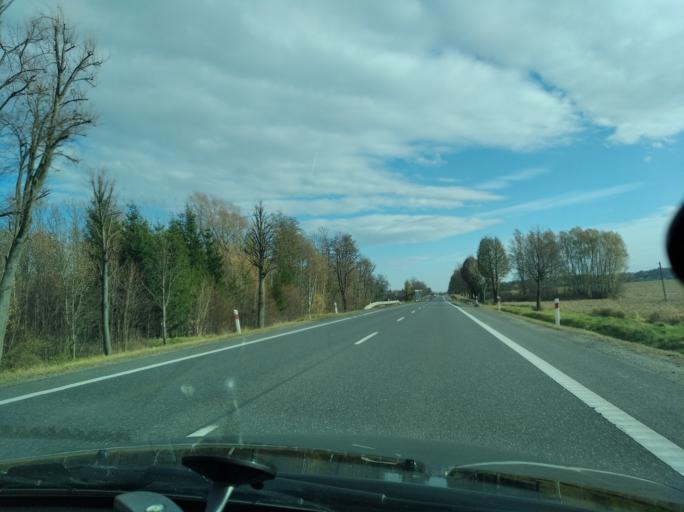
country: PL
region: Subcarpathian Voivodeship
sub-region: Powiat debicki
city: Brzeznica
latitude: 50.0608
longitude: 21.4929
